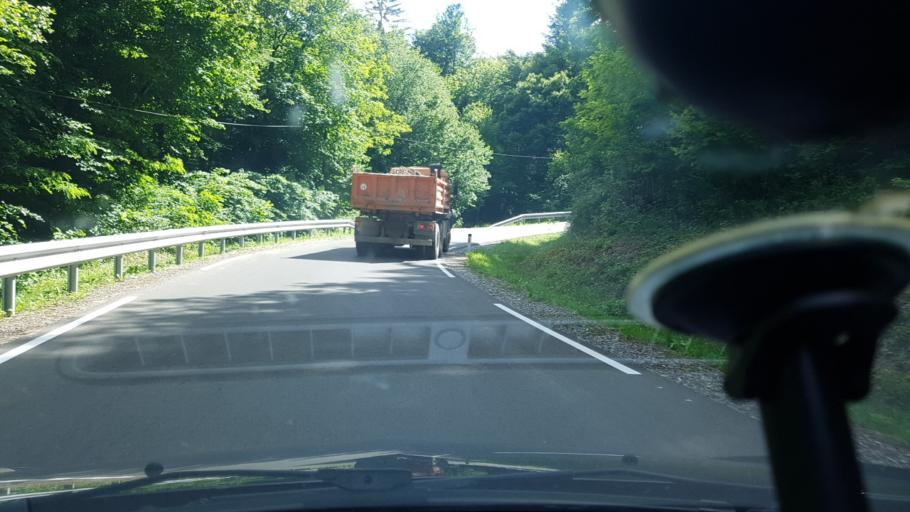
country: SI
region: Zetale
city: Zetale
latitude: 46.2636
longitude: 15.7679
